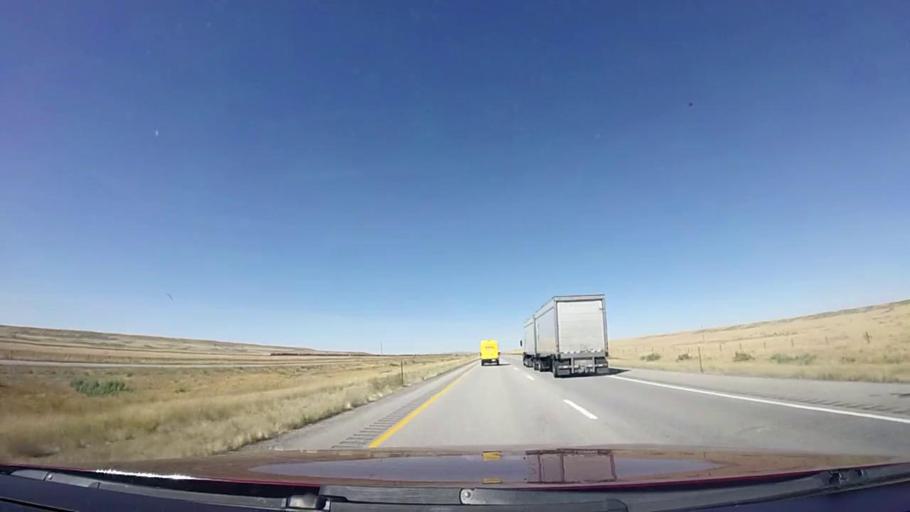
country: US
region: Wyoming
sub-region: Carbon County
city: Rawlins
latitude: 41.6599
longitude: -108.0746
